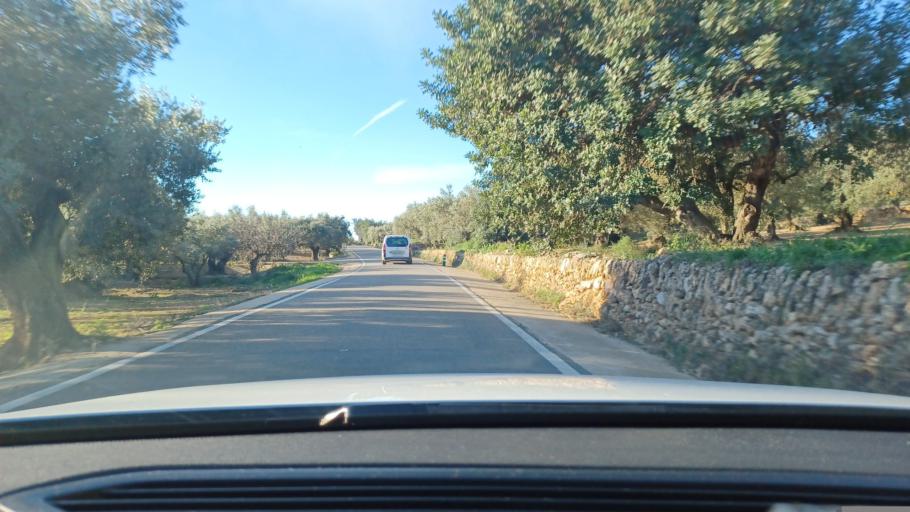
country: ES
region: Catalonia
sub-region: Provincia de Tarragona
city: Mas de Barberans
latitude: 40.7219
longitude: 0.3659
